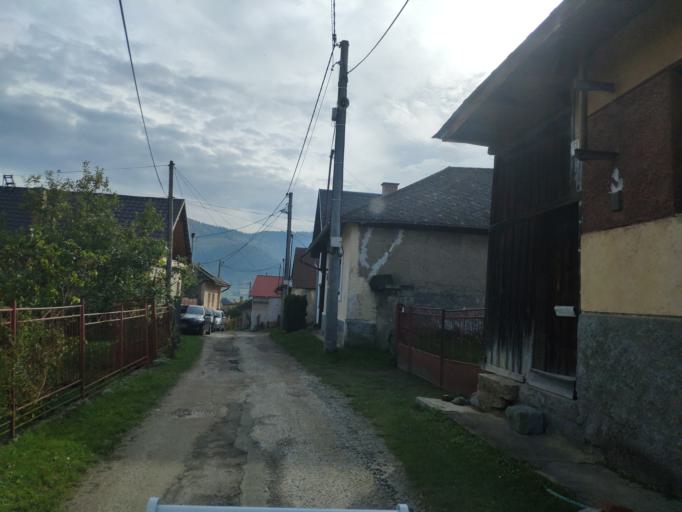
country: SK
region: Presovsky
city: Spisske Podhradie
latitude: 48.8177
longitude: 20.7128
